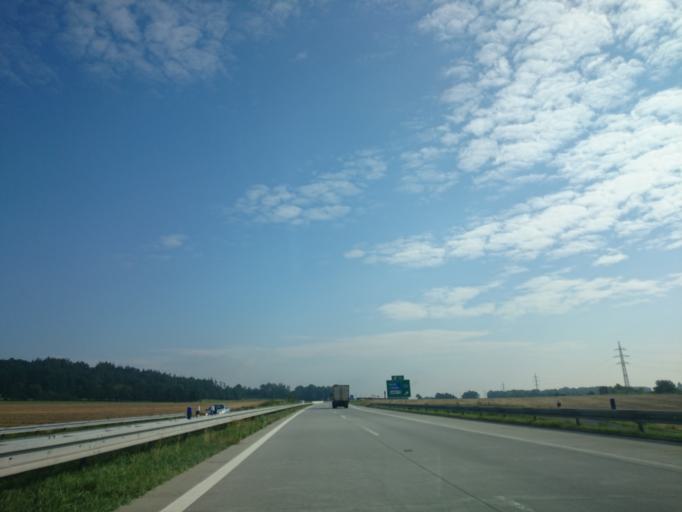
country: CZ
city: Bilovec
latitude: 49.7226
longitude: 18.0109
